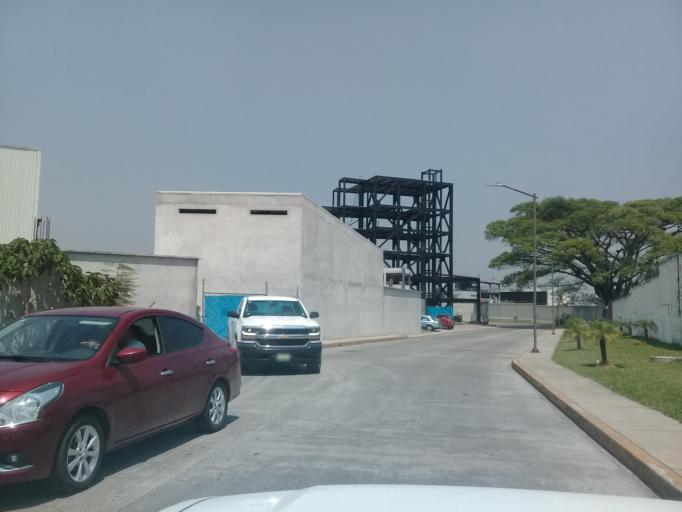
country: MX
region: Veracruz
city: Ixtac Zoquitlan
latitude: 18.8610
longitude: -97.0615
